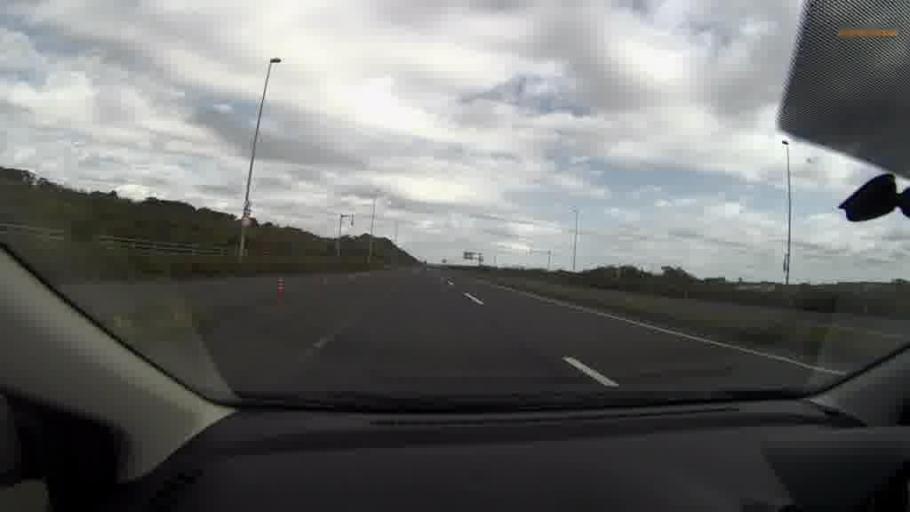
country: JP
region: Hokkaido
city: Kushiro
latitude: 43.0116
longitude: 144.2564
